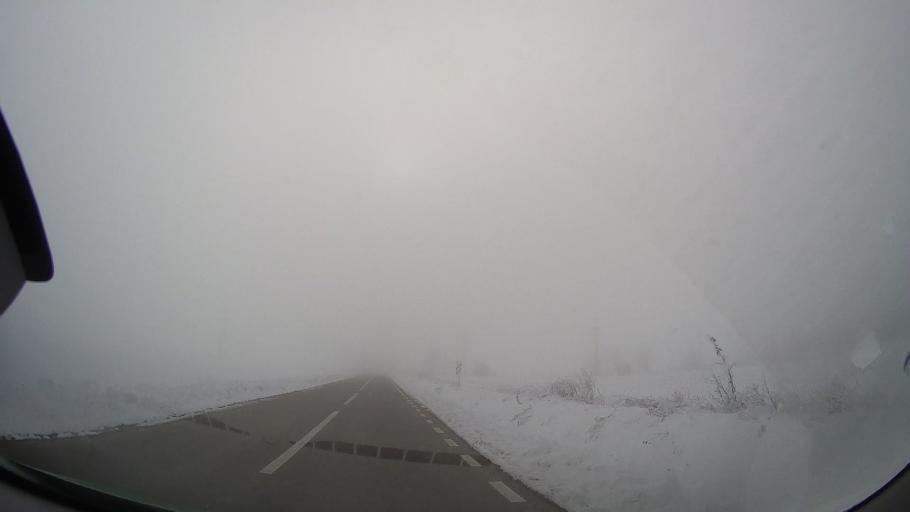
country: RO
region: Iasi
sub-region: Comuna Valea Seaca
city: Topile
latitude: 47.2769
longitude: 26.6708
